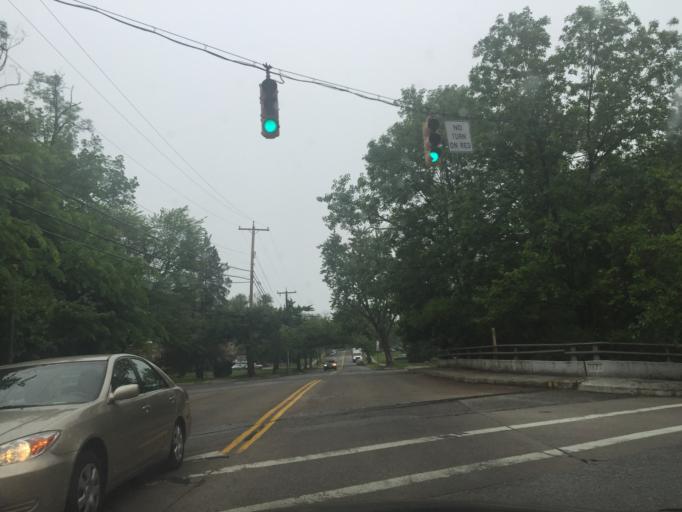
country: US
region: Maryland
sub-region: Baltimore County
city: Pikesville
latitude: 39.3646
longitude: -76.6974
